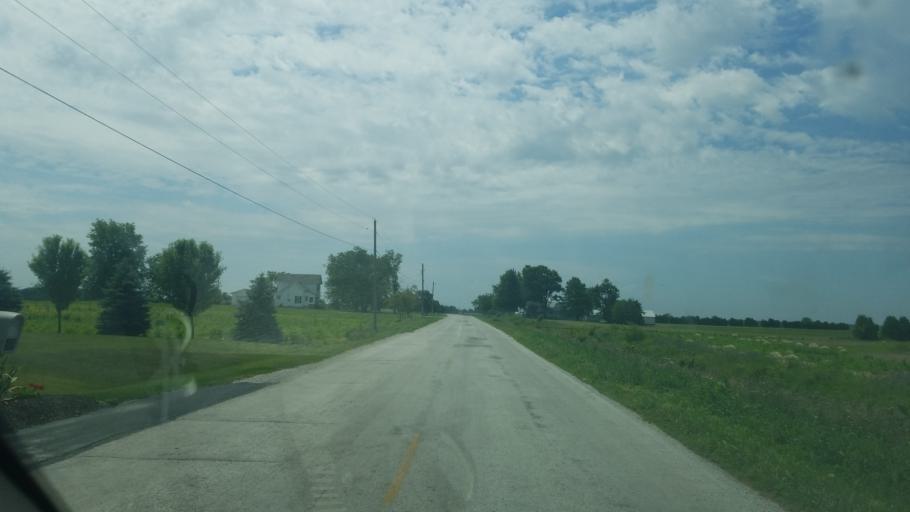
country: US
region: Ohio
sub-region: Wood County
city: Bowling Green
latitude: 41.2944
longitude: -83.5927
